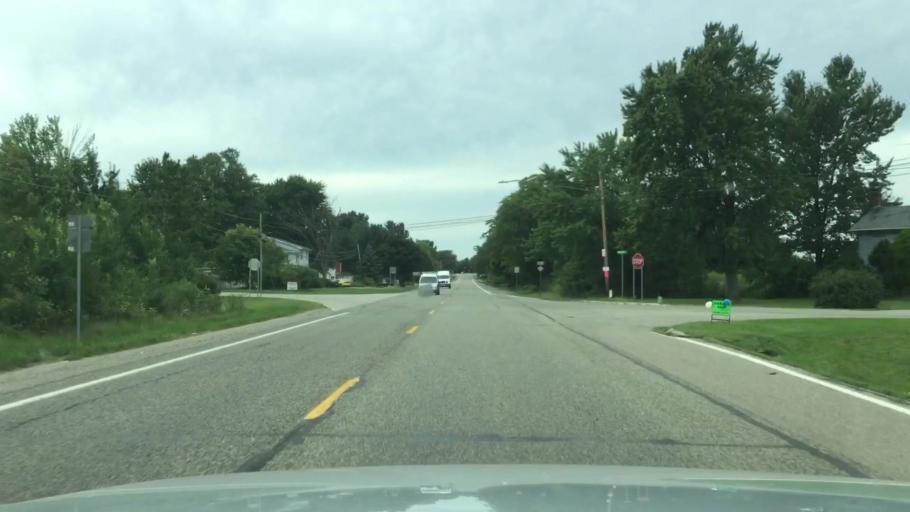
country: US
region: Michigan
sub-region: Shiawassee County
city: Durand
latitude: 42.9390
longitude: -84.0213
